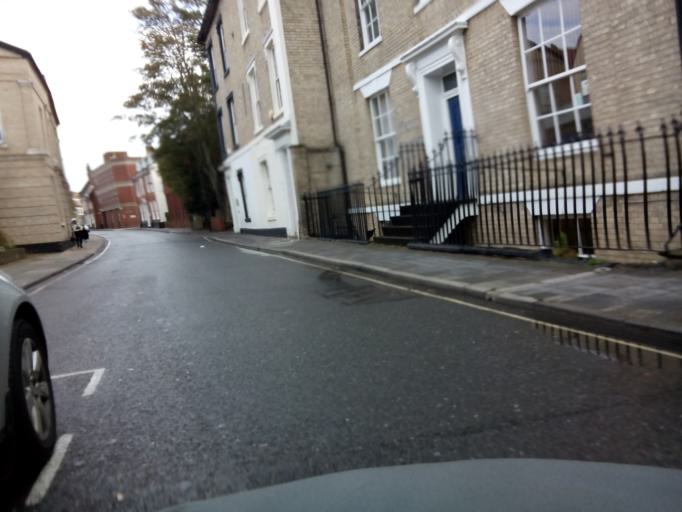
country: GB
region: England
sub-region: Suffolk
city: Ipswich
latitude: 52.0543
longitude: 1.1557
